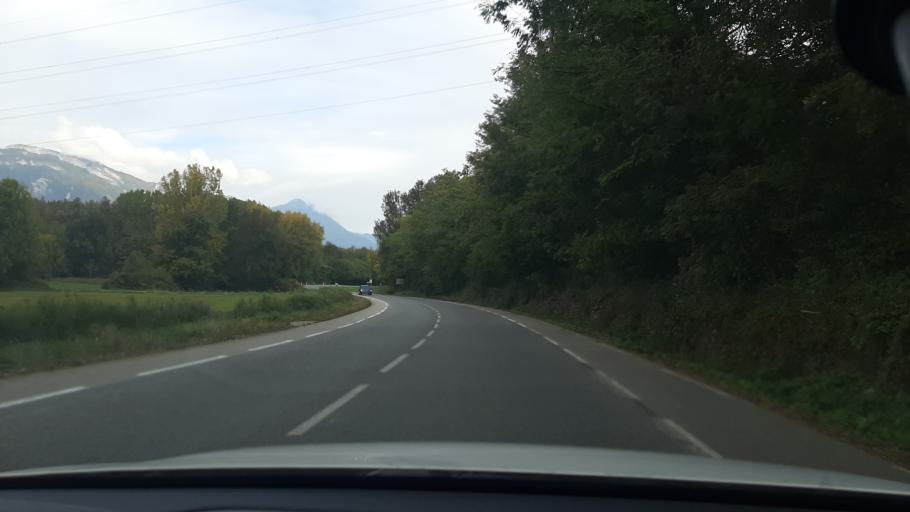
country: FR
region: Rhone-Alpes
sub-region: Departement de l'Isere
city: Pontcharra
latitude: 45.4553
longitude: 6.0475
